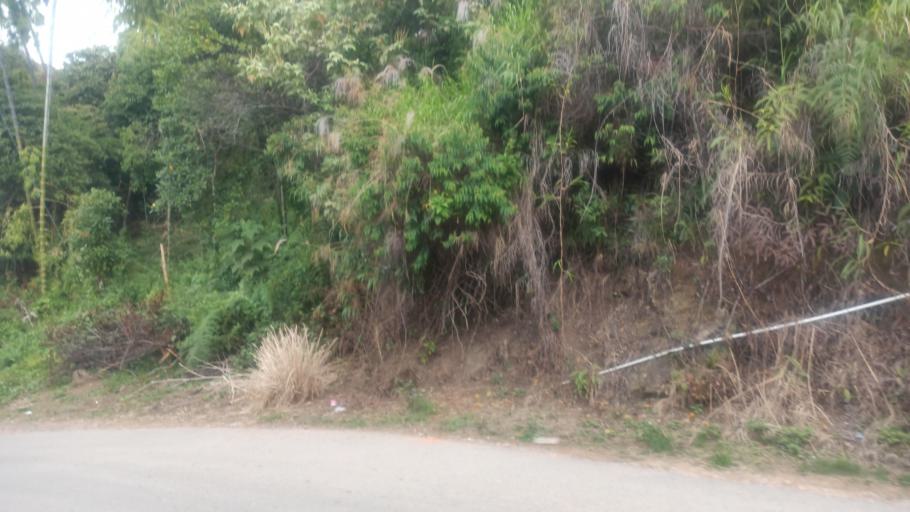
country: CO
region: Valle del Cauca
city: Jamundi
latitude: 3.2077
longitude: -76.6324
